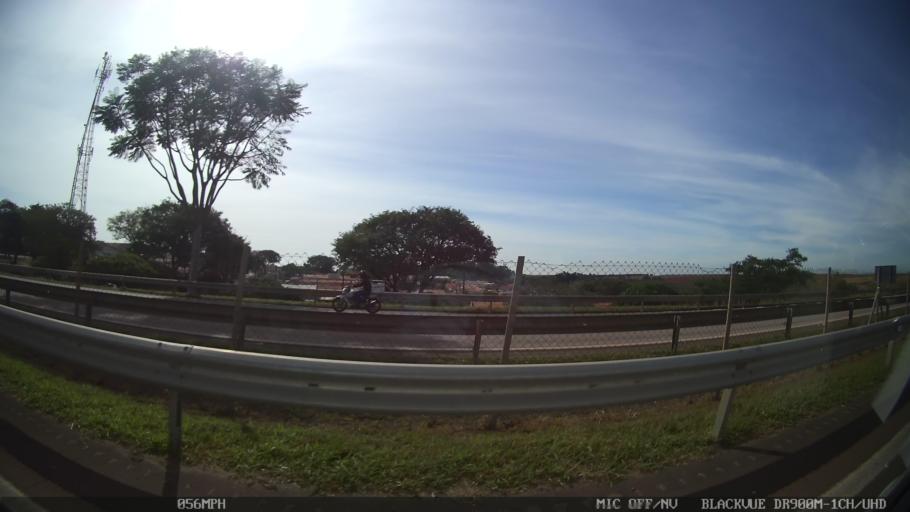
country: BR
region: Sao Paulo
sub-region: Rio Das Pedras
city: Rio das Pedras
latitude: -22.7745
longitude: -47.5918
